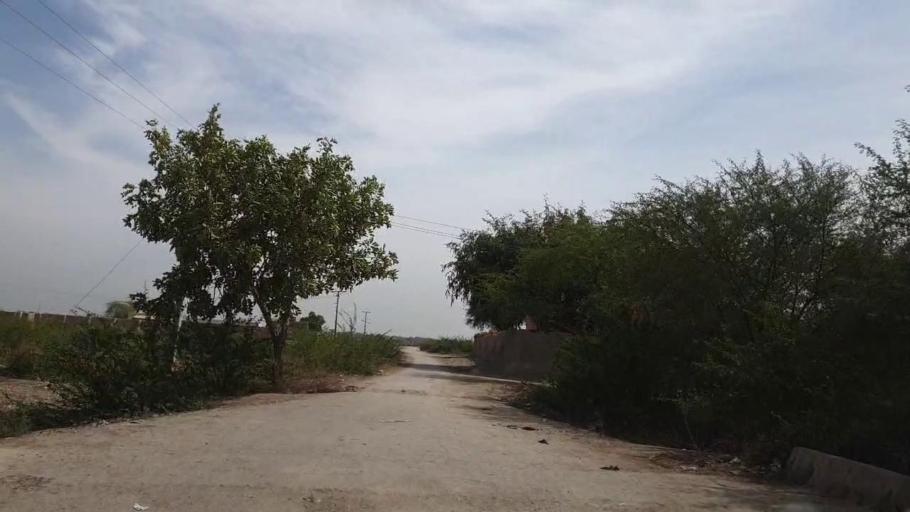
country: PK
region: Sindh
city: Kunri
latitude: 25.2078
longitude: 69.5865
